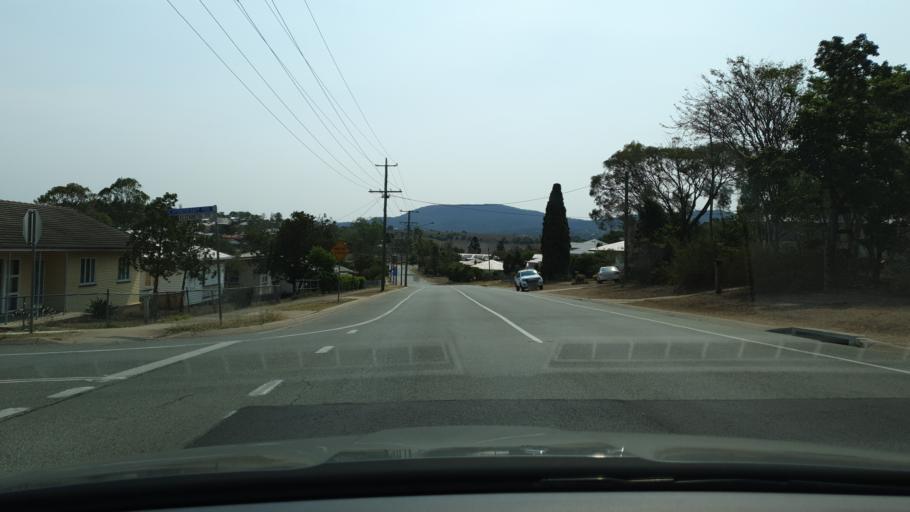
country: AU
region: Queensland
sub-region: Ipswich
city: Deebing Heights
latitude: -27.9926
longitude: 152.6869
